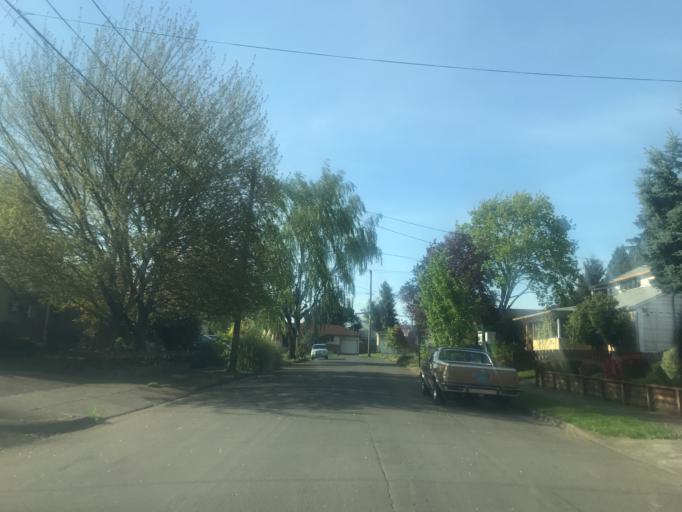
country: US
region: Oregon
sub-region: Multnomah County
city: Lents
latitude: 45.5023
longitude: -122.5975
